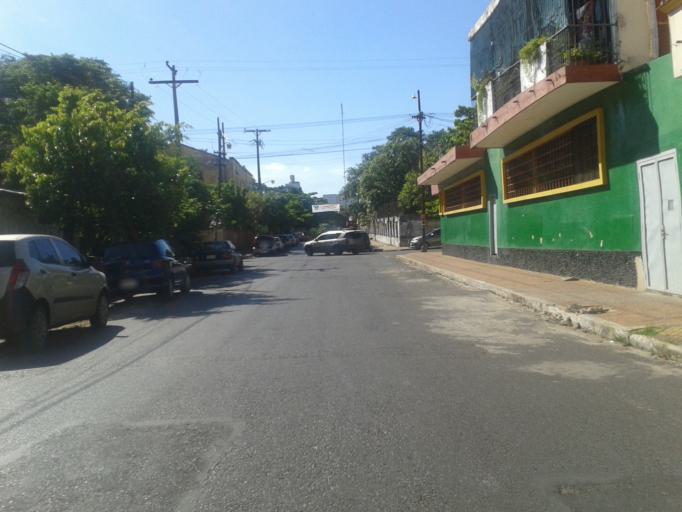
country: PY
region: Asuncion
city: Asuncion
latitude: -25.2929
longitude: -57.6411
